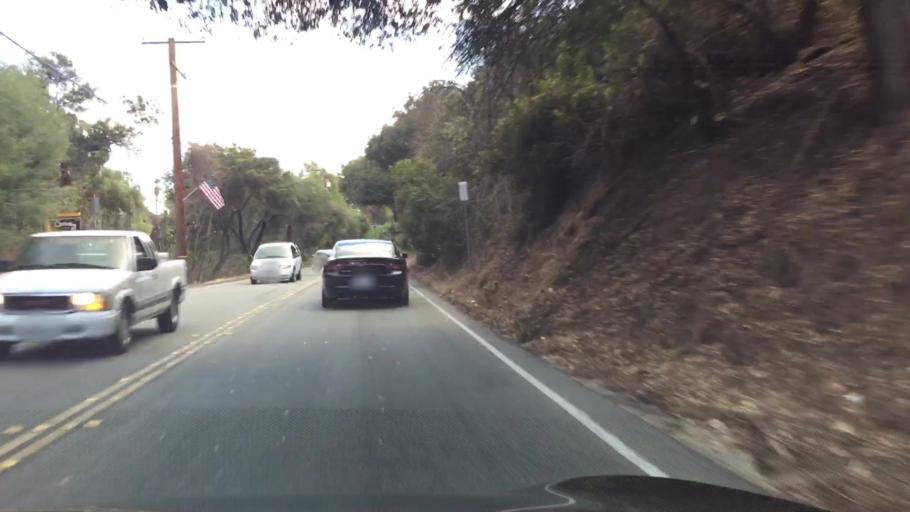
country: US
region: California
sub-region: Los Angeles County
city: La Habra Heights
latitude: 33.9703
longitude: -117.9639
